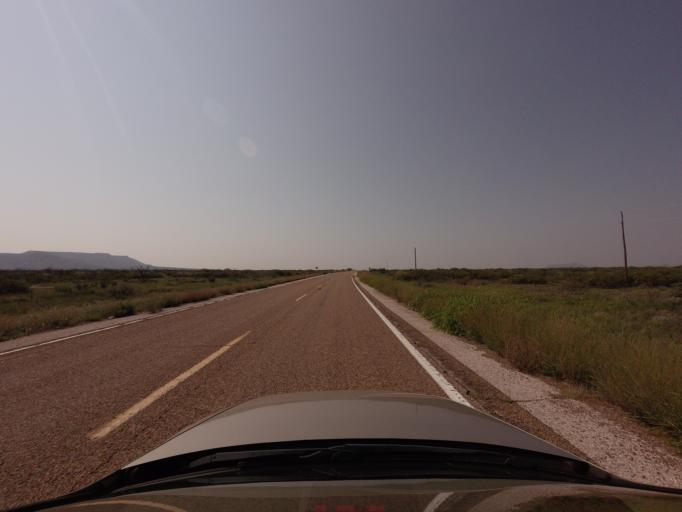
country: US
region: New Mexico
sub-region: Quay County
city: Tucumcari
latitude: 35.0195
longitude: -103.7379
